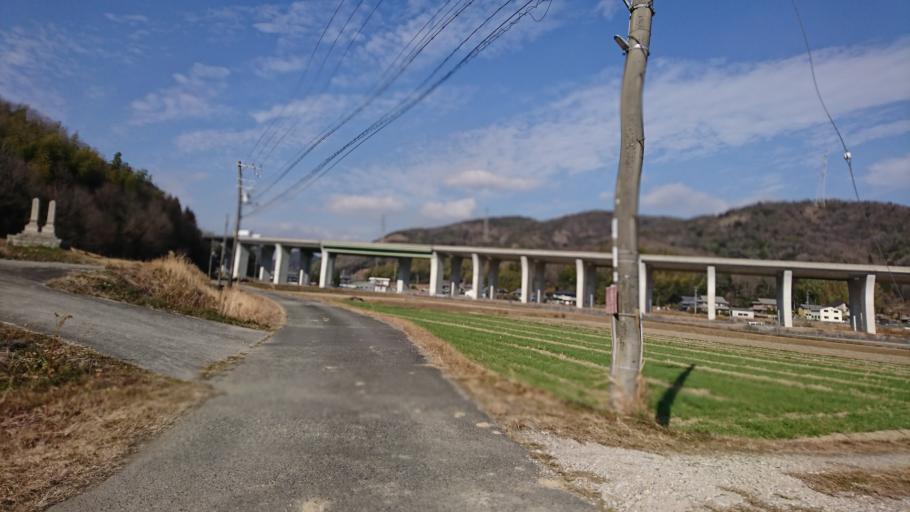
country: JP
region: Hyogo
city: Ono
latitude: 34.8372
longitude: 134.8648
